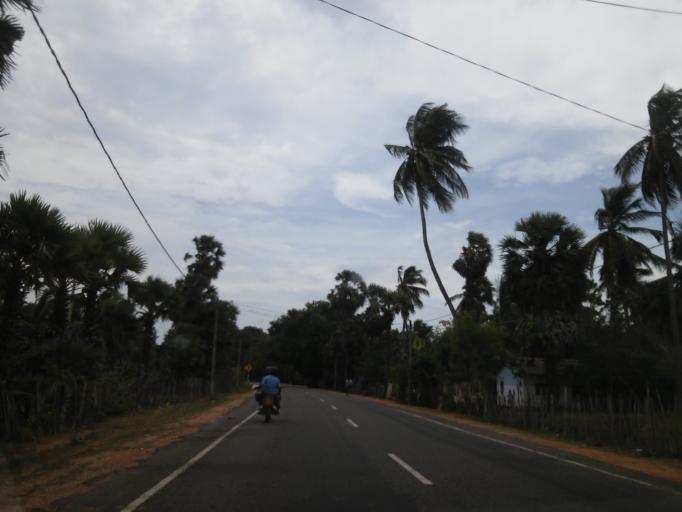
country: LK
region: Eastern Province
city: Trincomalee
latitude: 8.6942
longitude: 81.1833
